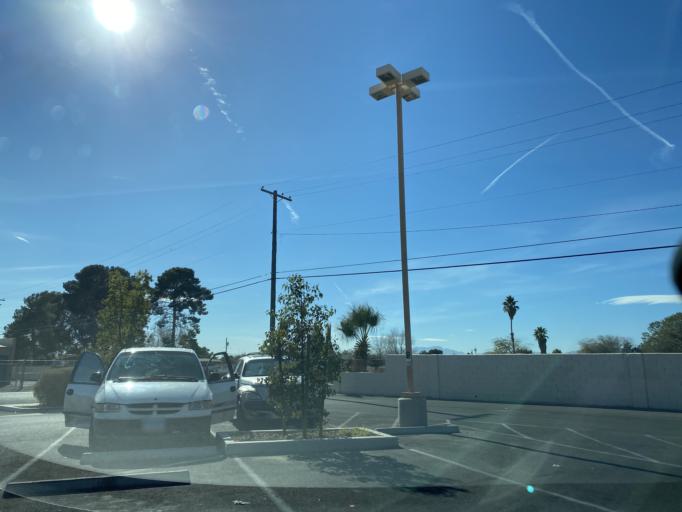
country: US
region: Nevada
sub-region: Clark County
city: Sunrise Manor
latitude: 36.1872
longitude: -115.0631
